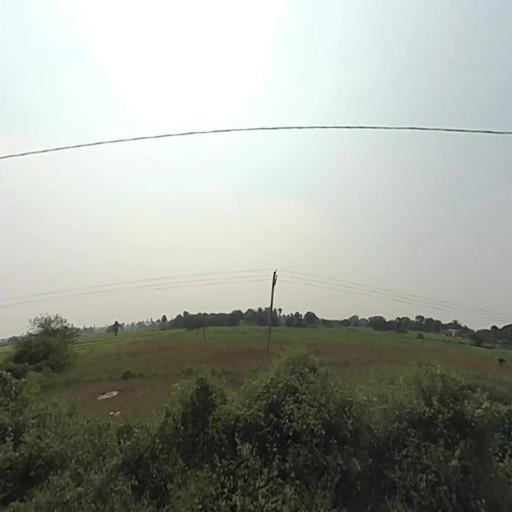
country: IN
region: Telangana
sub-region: Nalgonda
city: Nalgonda
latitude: 17.1827
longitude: 79.1250
